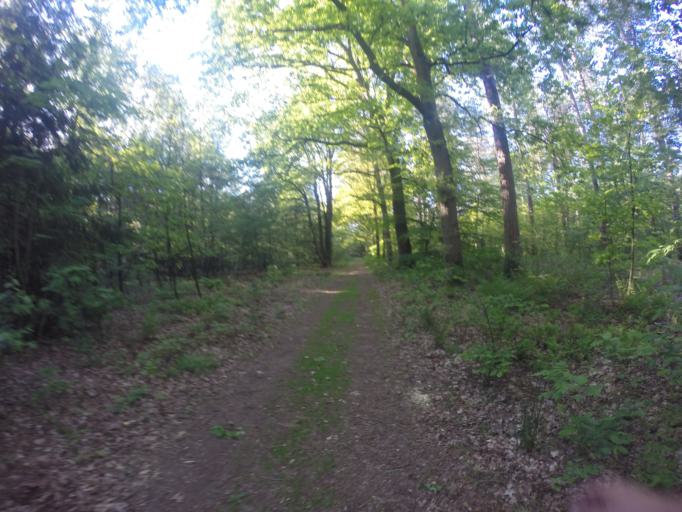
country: NL
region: Gelderland
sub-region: Gemeente Montferland
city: s-Heerenberg
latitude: 51.8978
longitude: 6.2172
